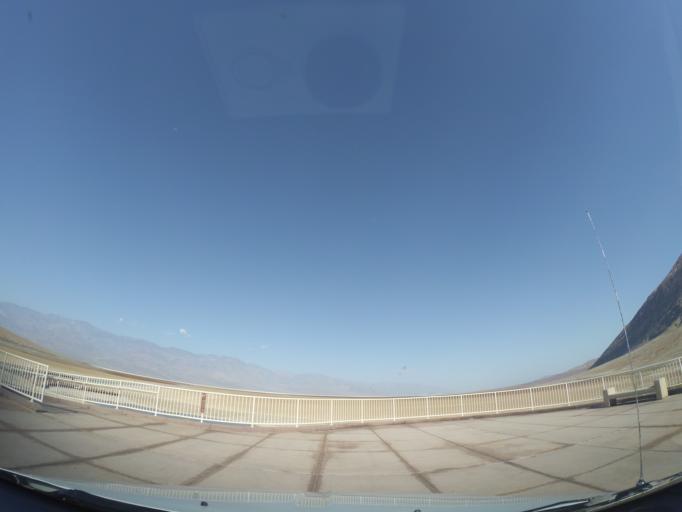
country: US
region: Nevada
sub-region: Nye County
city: Beatty
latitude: 36.2311
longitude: -116.7750
